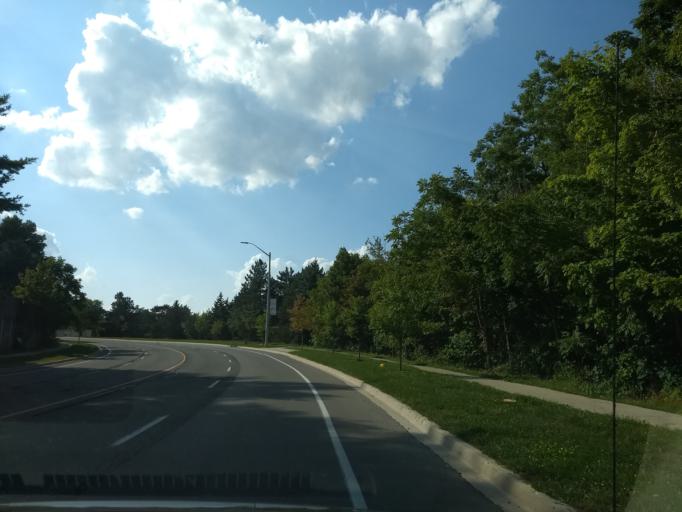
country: CA
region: Ontario
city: Mississauga
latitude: 43.5461
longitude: -79.6726
